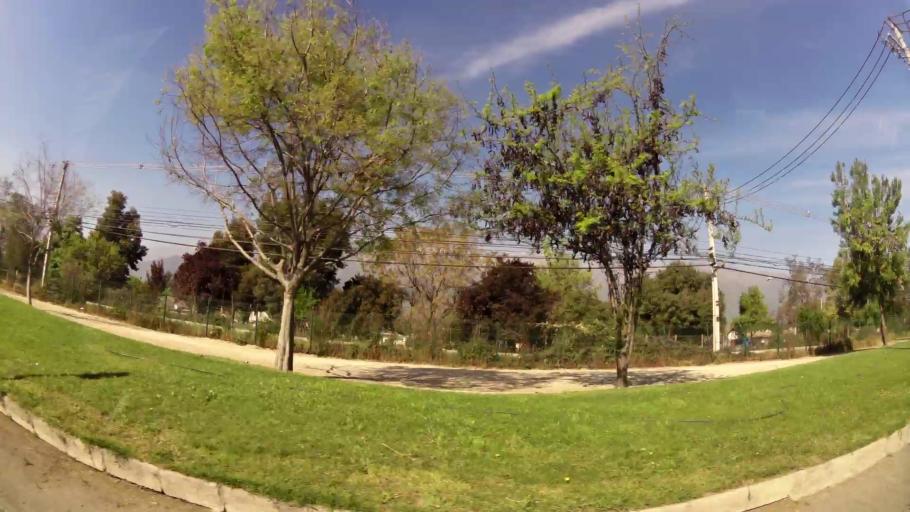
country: CL
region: Santiago Metropolitan
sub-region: Provincia de Santiago
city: Villa Presidente Frei, Nunoa, Santiago, Chile
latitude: -33.4817
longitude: -70.5581
